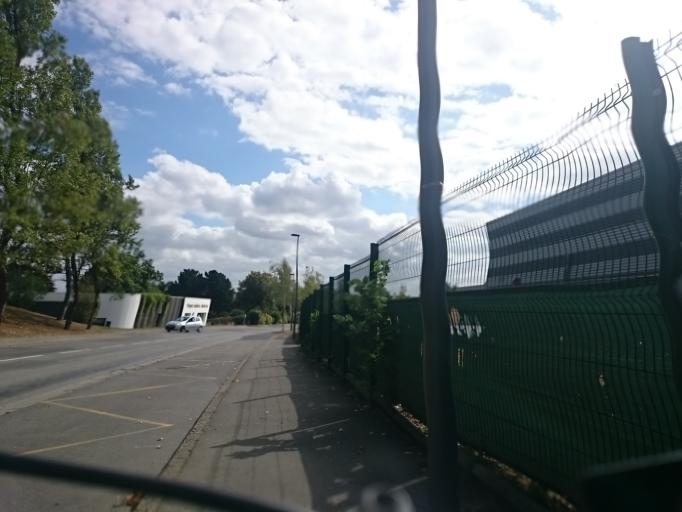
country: FR
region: Brittany
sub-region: Departement d'Ille-et-Vilaine
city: Cesson-Sevigne
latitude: 48.1287
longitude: -1.5975
